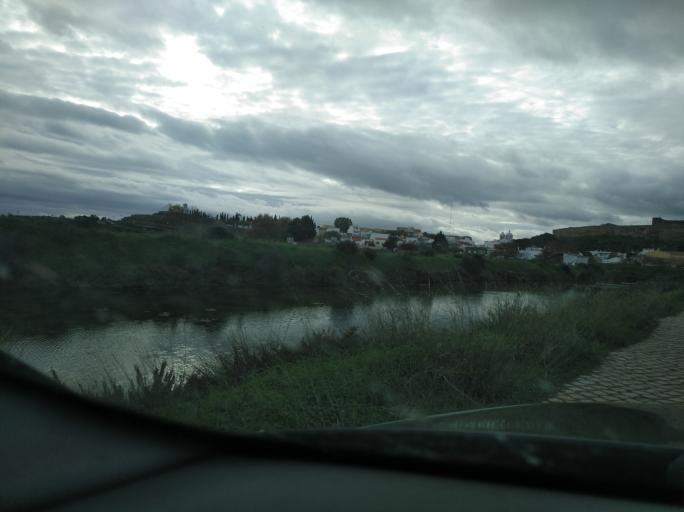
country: PT
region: Faro
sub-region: Castro Marim
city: Castro Marim
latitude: 37.2186
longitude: -7.4362
